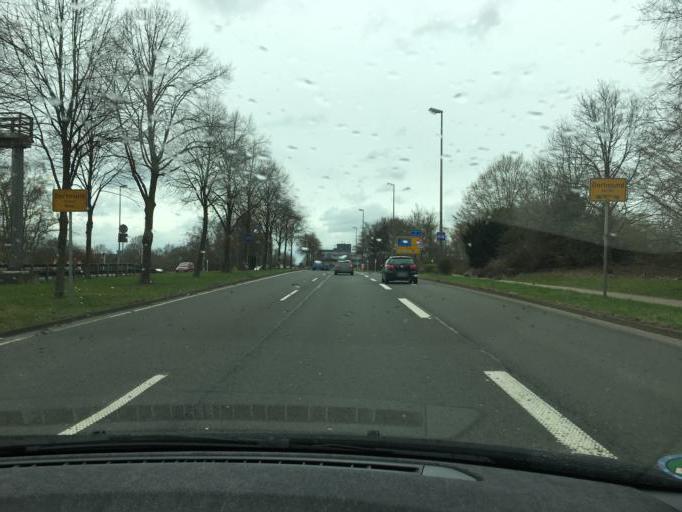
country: DE
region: North Rhine-Westphalia
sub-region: Regierungsbezirk Arnsberg
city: Dortmund
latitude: 51.4966
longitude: 7.4688
